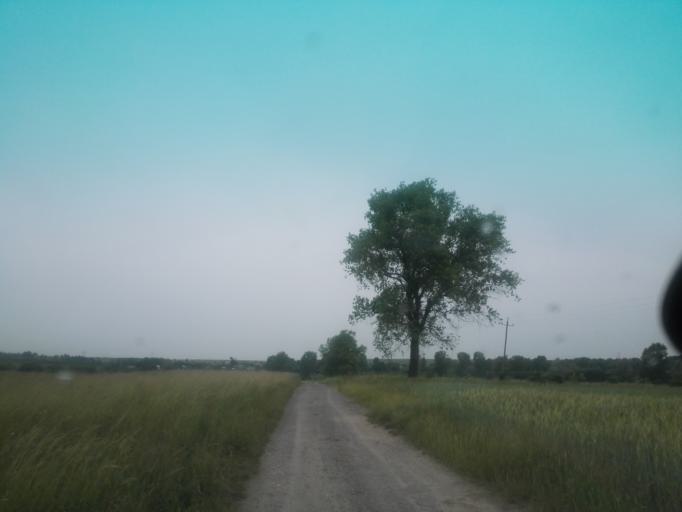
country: PL
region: Silesian Voivodeship
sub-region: Powiat czestochowski
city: Mstow
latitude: 50.7868
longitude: 19.3212
